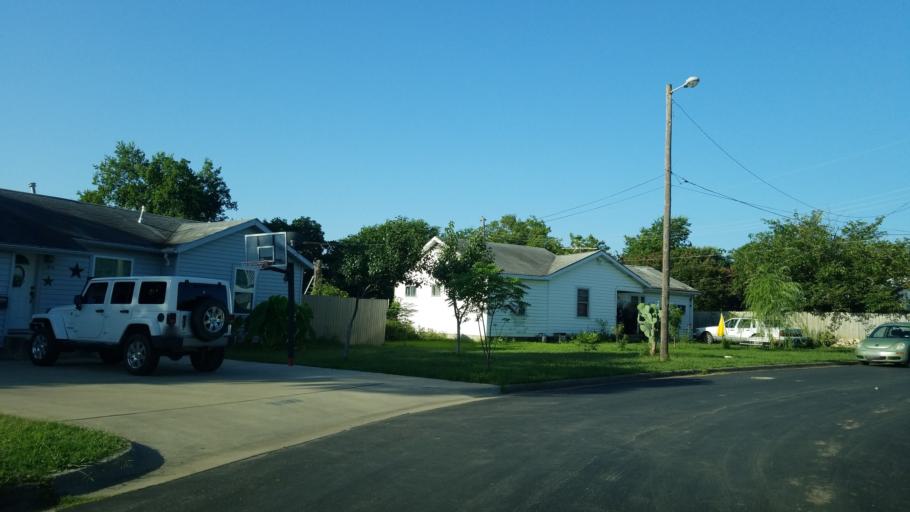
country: US
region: Texas
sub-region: Dallas County
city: Grand Prairie
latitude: 32.7528
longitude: -96.9502
